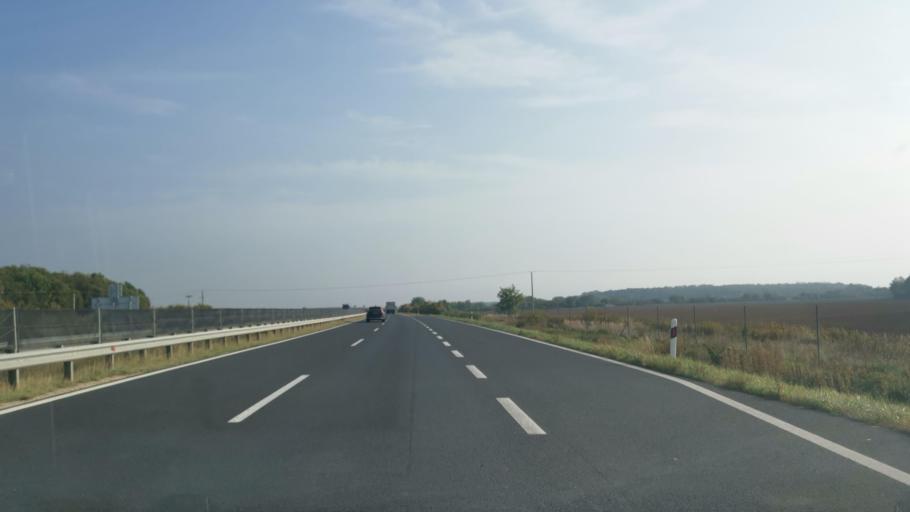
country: HU
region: Vas
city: Vep
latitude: 47.2591
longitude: 16.7318
